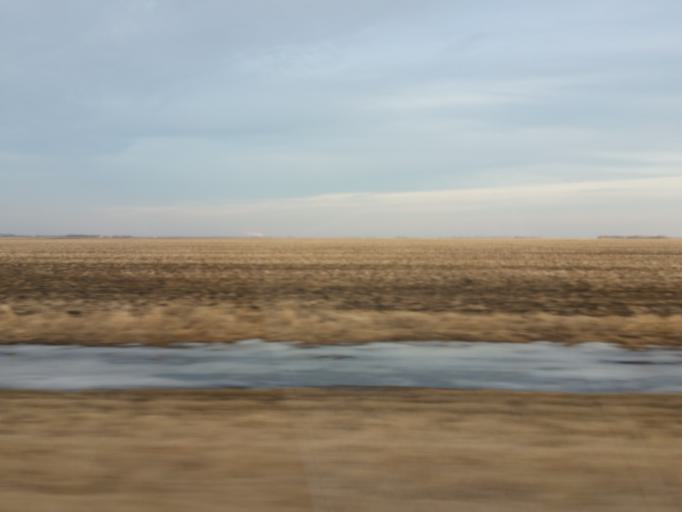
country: US
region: North Dakota
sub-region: Traill County
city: Mayville
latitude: 47.4083
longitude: -97.3262
